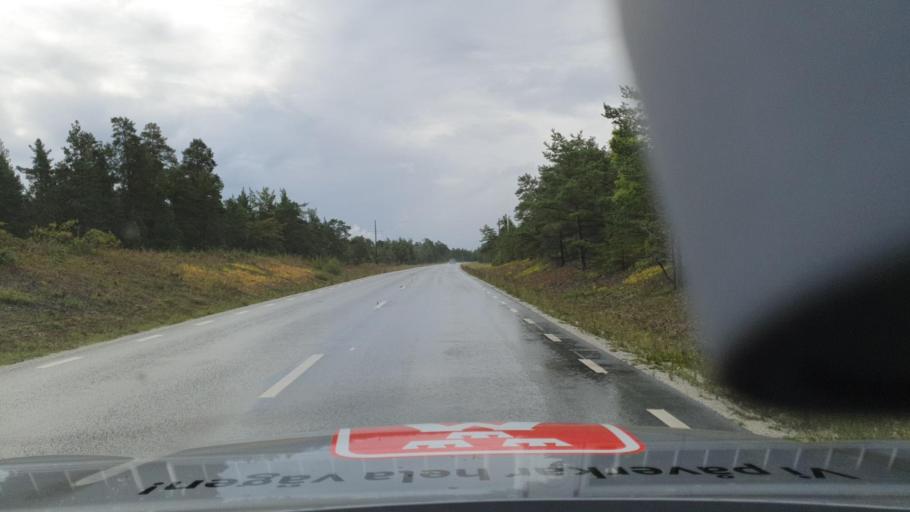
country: SE
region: Gotland
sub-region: Gotland
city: Slite
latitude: 57.7377
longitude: 18.7908
